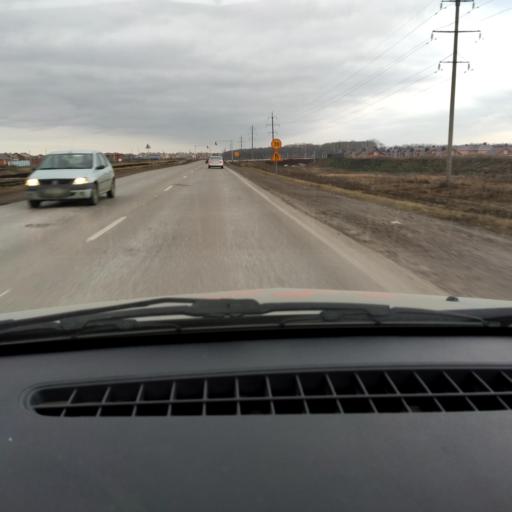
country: RU
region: Bashkortostan
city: Ufa
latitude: 54.6321
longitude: 55.9084
